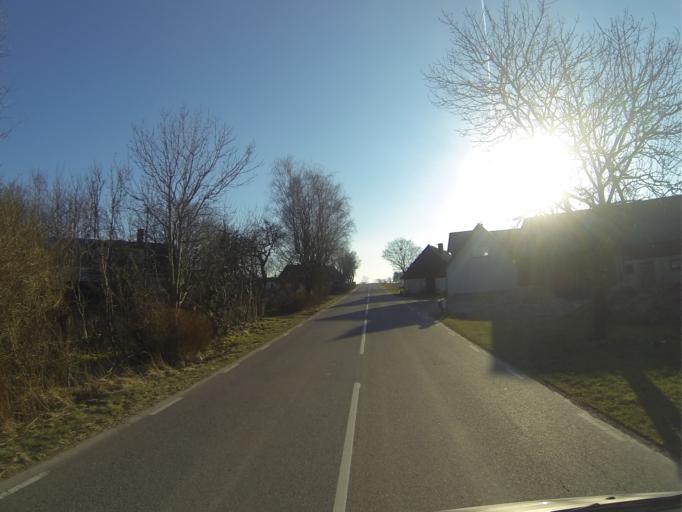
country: SE
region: Skane
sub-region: Hoors Kommun
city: Loberod
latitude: 55.7886
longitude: 13.5340
